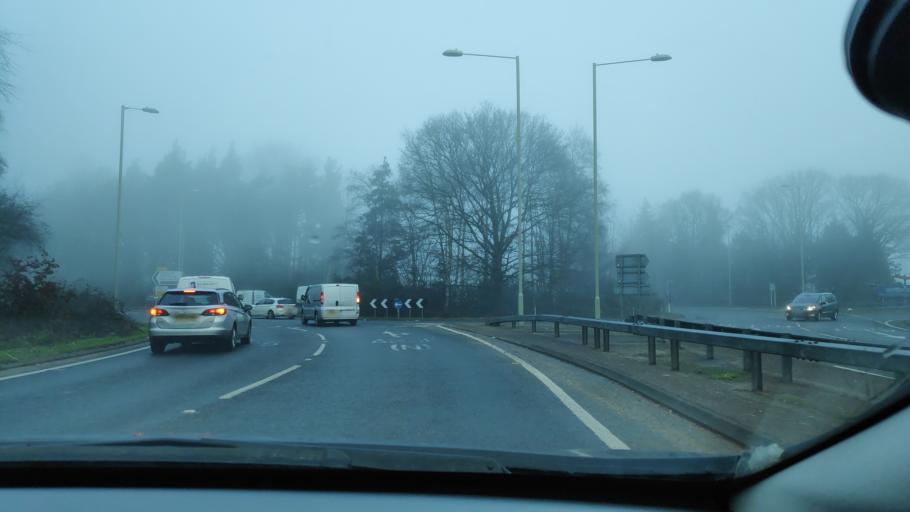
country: GB
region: England
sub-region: Hampshire
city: Farnborough
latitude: 51.2748
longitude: -0.7365
